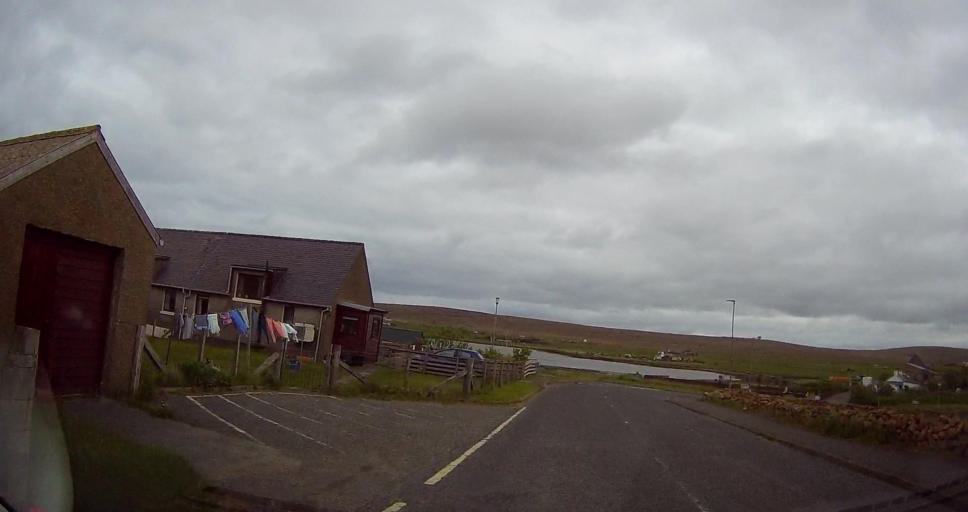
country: GB
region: Scotland
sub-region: Shetland Islands
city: Shetland
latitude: 60.7592
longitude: -0.8587
